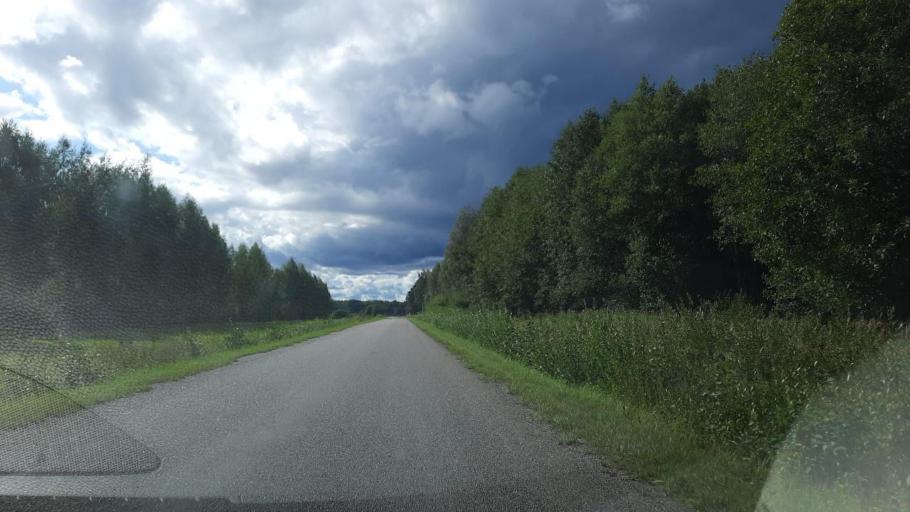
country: EE
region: Paernumaa
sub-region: Vaendra vald (alev)
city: Vandra
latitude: 58.4916
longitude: 24.9619
